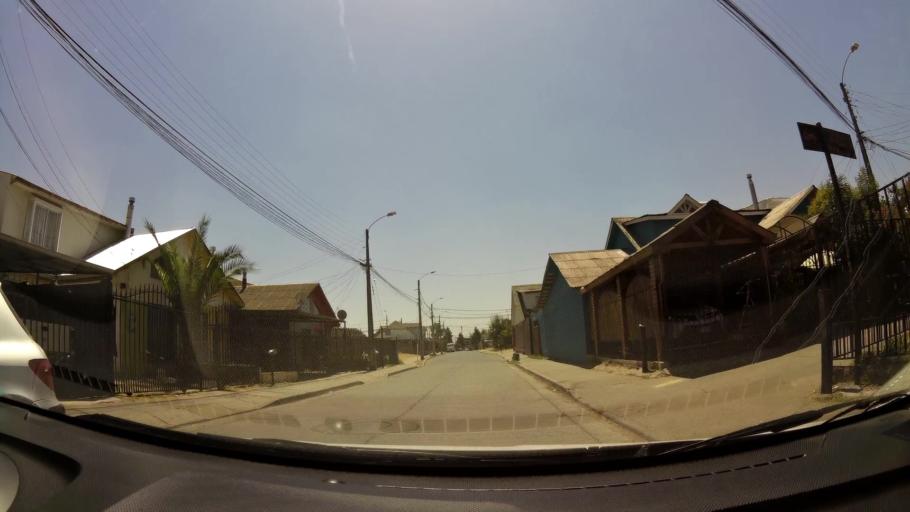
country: CL
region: Maule
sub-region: Provincia de Talca
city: Talca
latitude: -35.4364
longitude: -71.6339
